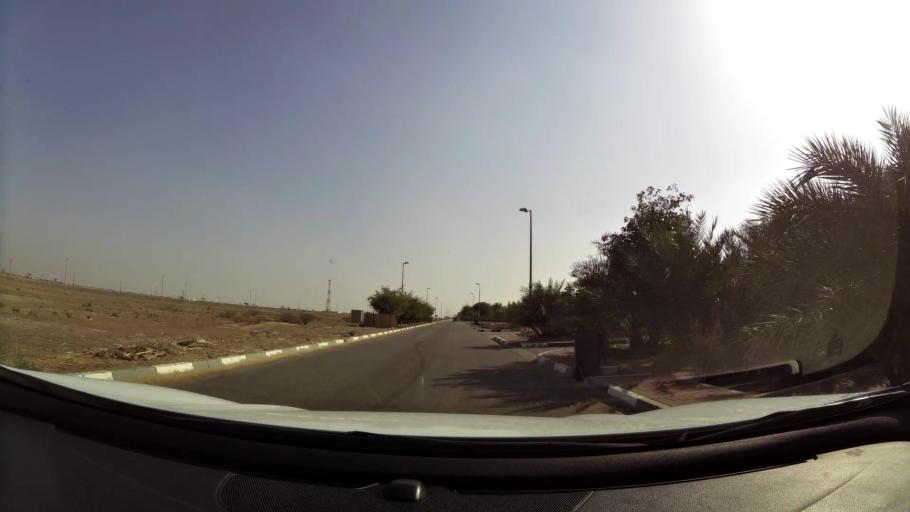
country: AE
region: Abu Dhabi
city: Al Ain
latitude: 24.0891
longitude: 55.8727
